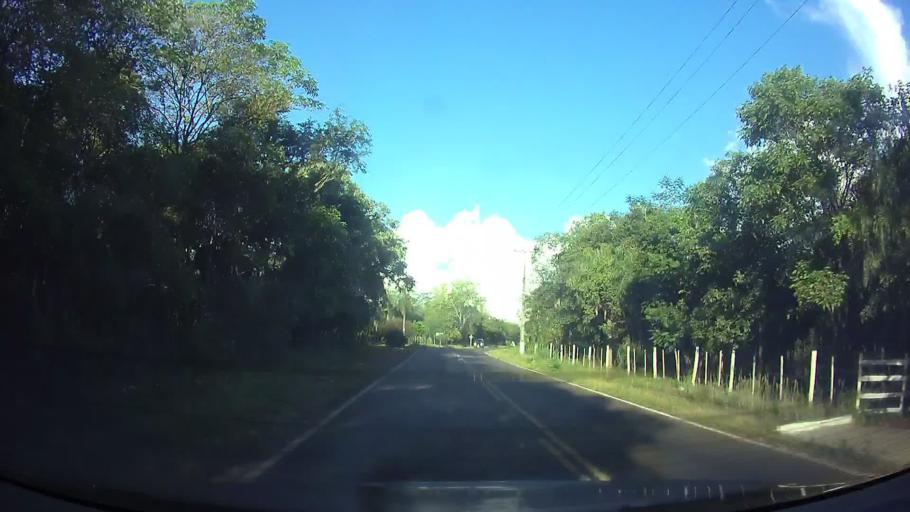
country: PY
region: Cordillera
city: Emboscada
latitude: -25.2045
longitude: -57.3434
